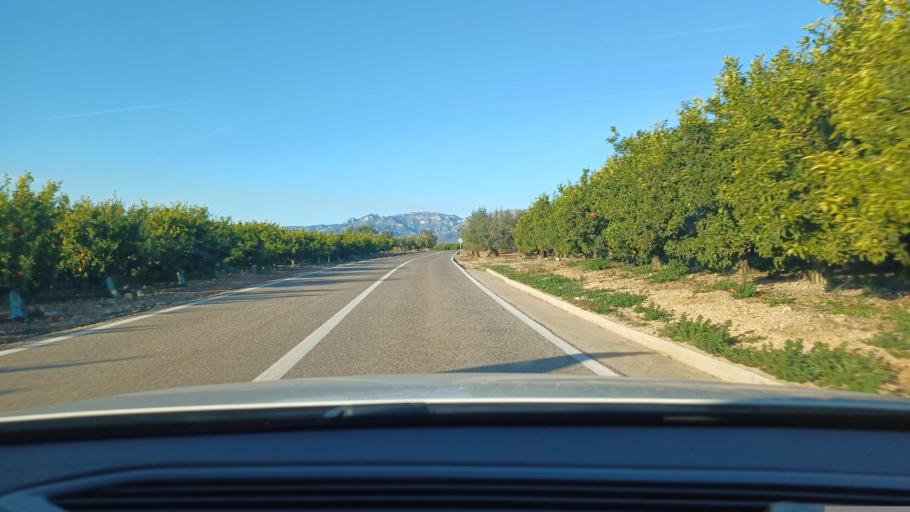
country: ES
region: Catalonia
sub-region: Provincia de Tarragona
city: Santa Barbara
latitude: 40.7198
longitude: 0.4642
